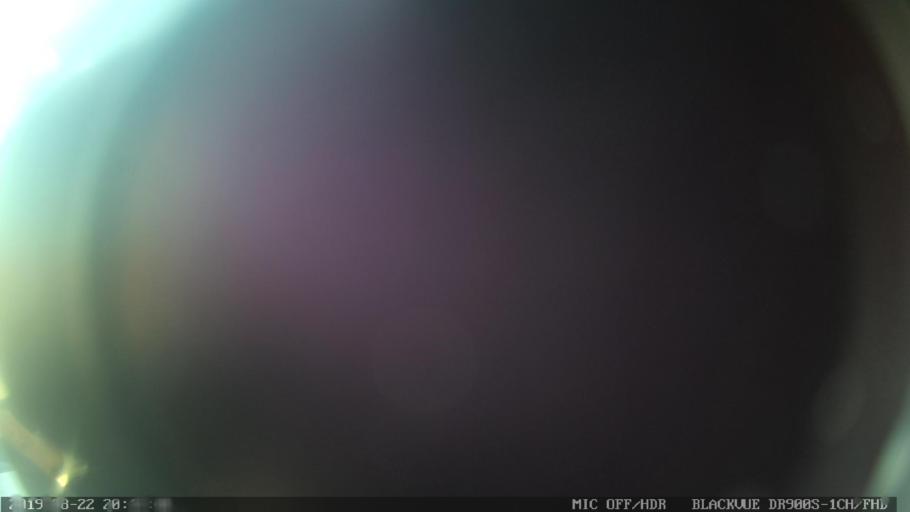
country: PT
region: Guarda
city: Alcains
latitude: 39.9222
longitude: -7.4439
